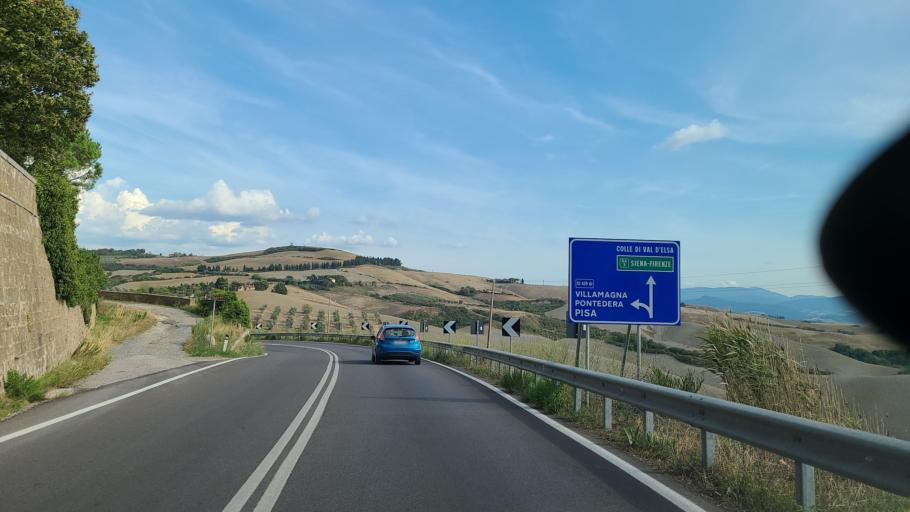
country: IT
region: Tuscany
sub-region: Province of Pisa
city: Volterra
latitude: 43.3929
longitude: 10.8941
